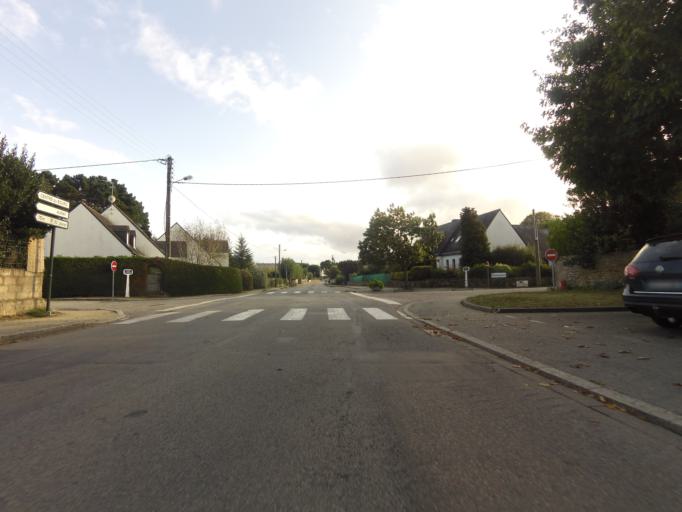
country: FR
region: Brittany
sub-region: Departement du Morbihan
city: Carnac
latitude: 47.5832
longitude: -3.0751
